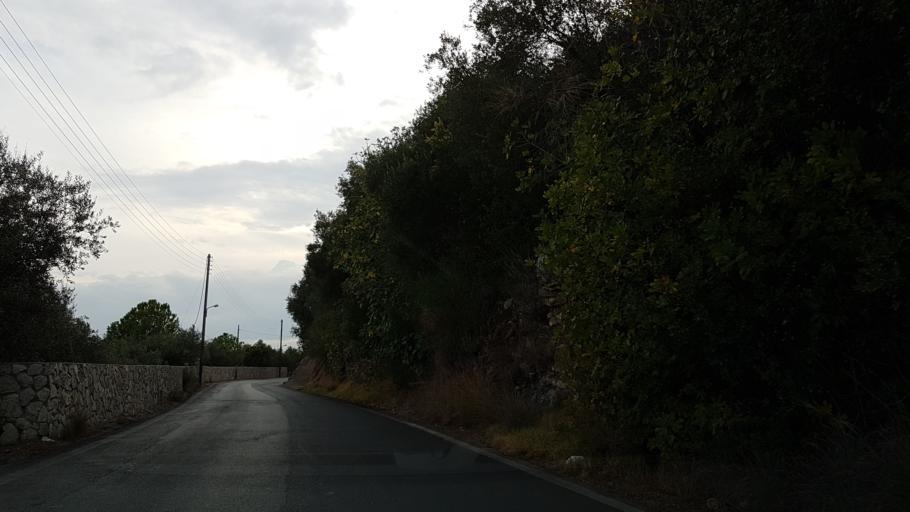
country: GR
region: Ionian Islands
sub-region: Nomos Kerkyras
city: Kontokali
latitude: 39.7308
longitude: 19.9168
